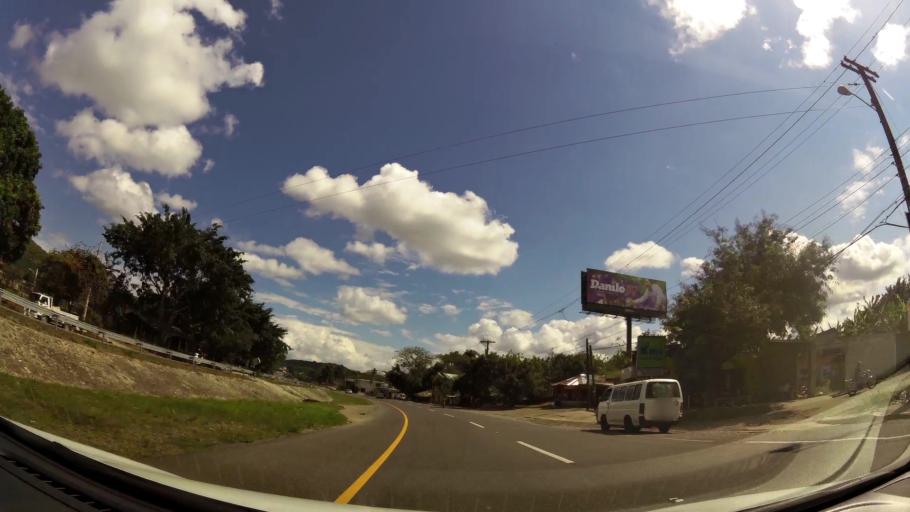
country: DO
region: La Vega
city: Rio Verde Arriba
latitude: 19.3022
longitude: -70.5842
